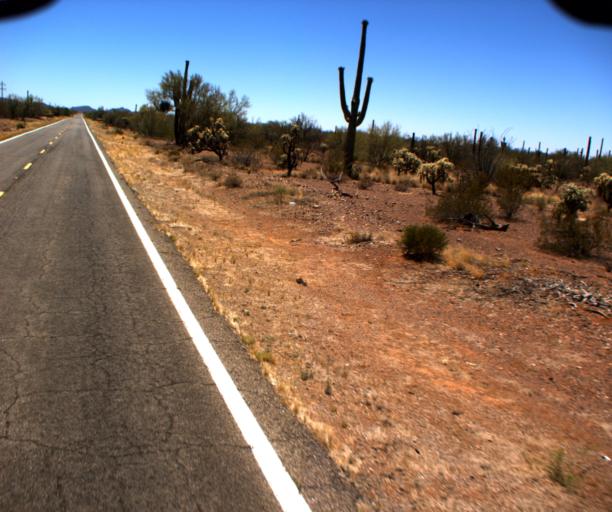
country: US
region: Arizona
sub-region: Pima County
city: Sells
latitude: 32.0464
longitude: -112.0225
